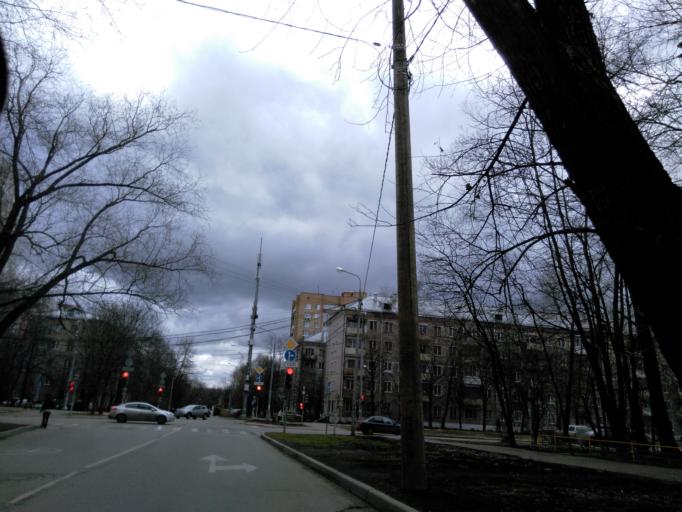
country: RU
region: Moskovskaya
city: Koptevo
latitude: 55.8353
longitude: 37.5286
